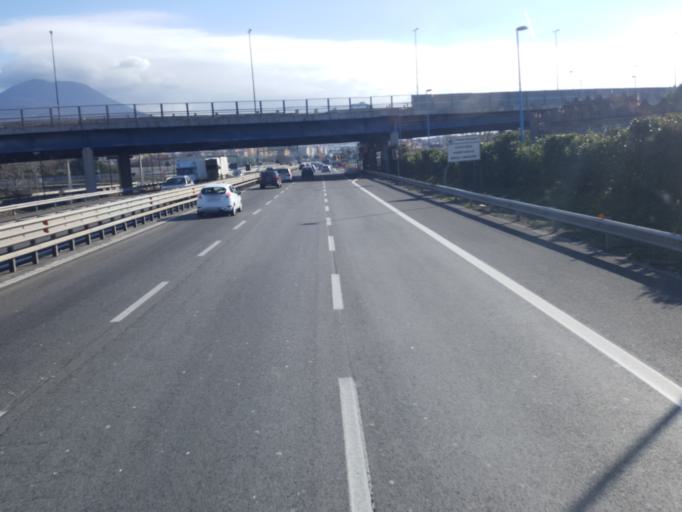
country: IT
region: Campania
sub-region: Provincia di Napoli
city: San Giorgio a Cremano
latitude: 40.8405
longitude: 14.3306
